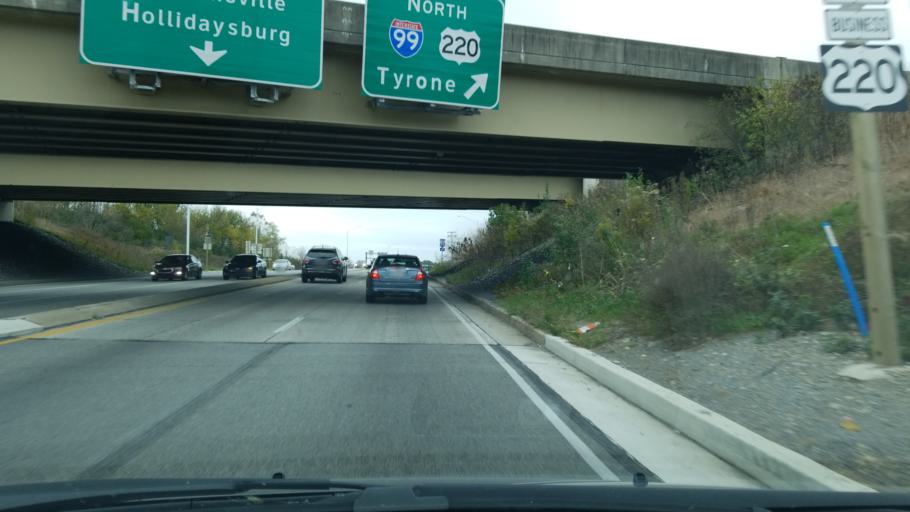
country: US
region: Pennsylvania
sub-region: Blair County
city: Lakemont
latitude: 40.4658
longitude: -78.4079
